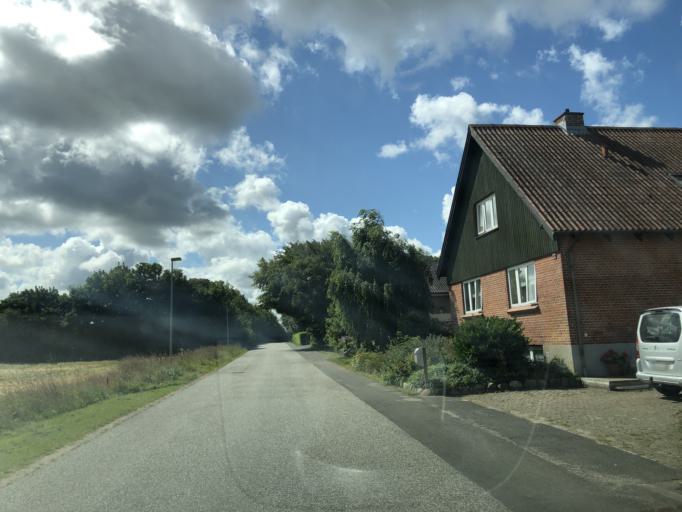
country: DK
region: Central Jutland
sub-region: Struer Kommune
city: Struer
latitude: 56.4642
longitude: 8.5225
